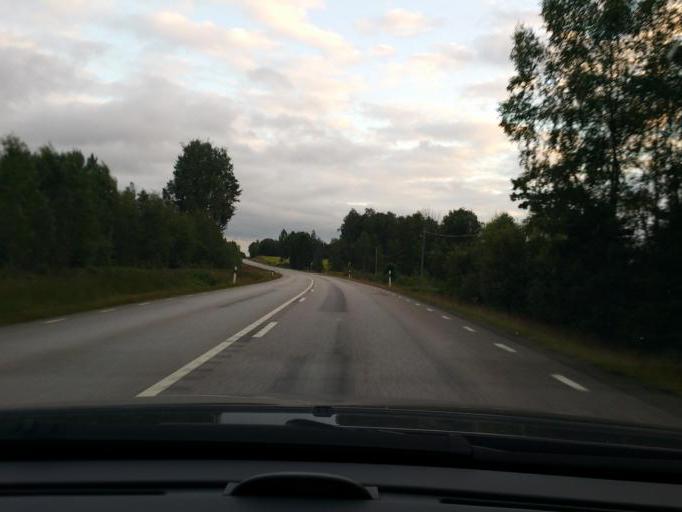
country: SE
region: Kronoberg
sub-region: Vaxjo Kommun
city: Lammhult
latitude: 57.0824
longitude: 14.6194
